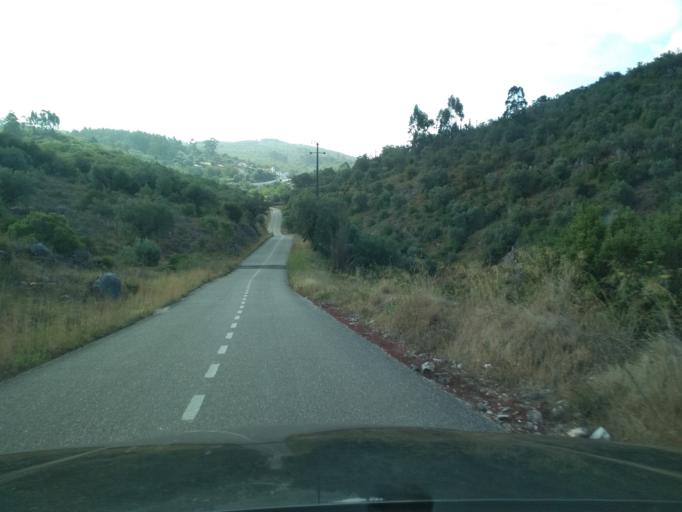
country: PT
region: Coimbra
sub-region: Condeixa-A-Nova
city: Condeixa-a-Nova
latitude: 40.0733
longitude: -8.5029
